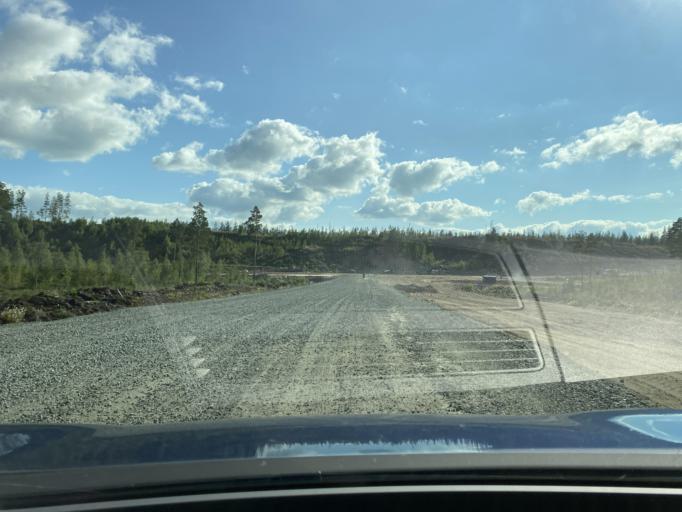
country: FI
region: Kymenlaakso
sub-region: Kouvola
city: Iitti
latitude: 60.8773
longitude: 26.4928
